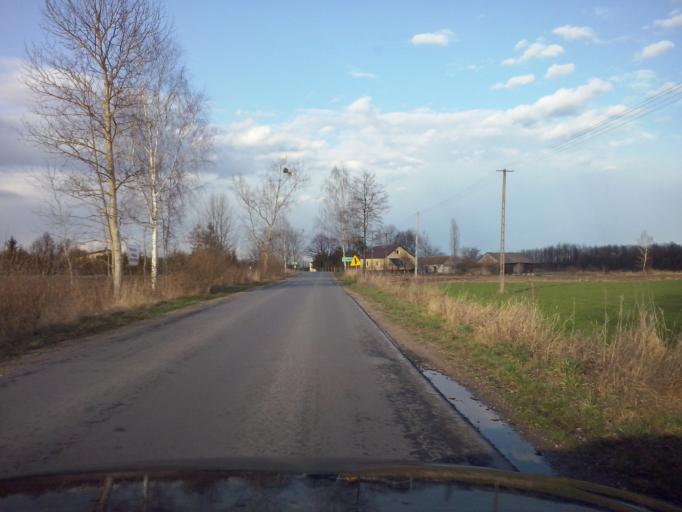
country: PL
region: Lublin Voivodeship
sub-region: Powiat chelmski
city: Ruda-Huta
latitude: 51.1952
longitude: 23.5350
